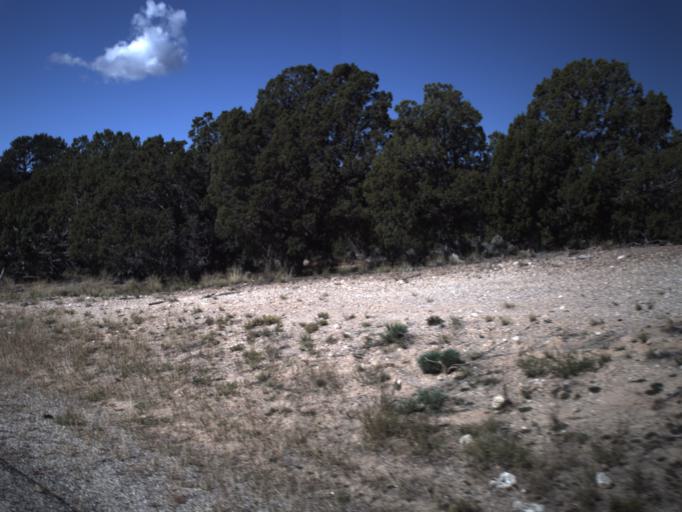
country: US
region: Utah
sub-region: Iron County
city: Cedar City
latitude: 37.6427
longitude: -113.2510
